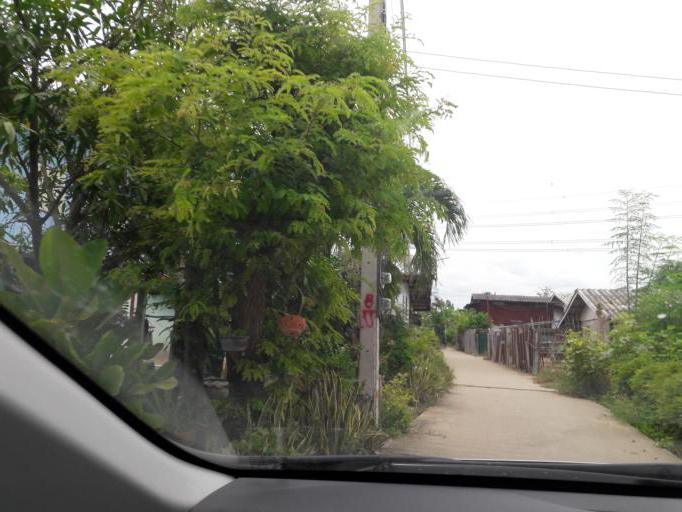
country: TH
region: Samut Sakhon
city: Ban Phaeo
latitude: 13.6262
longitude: 100.0201
